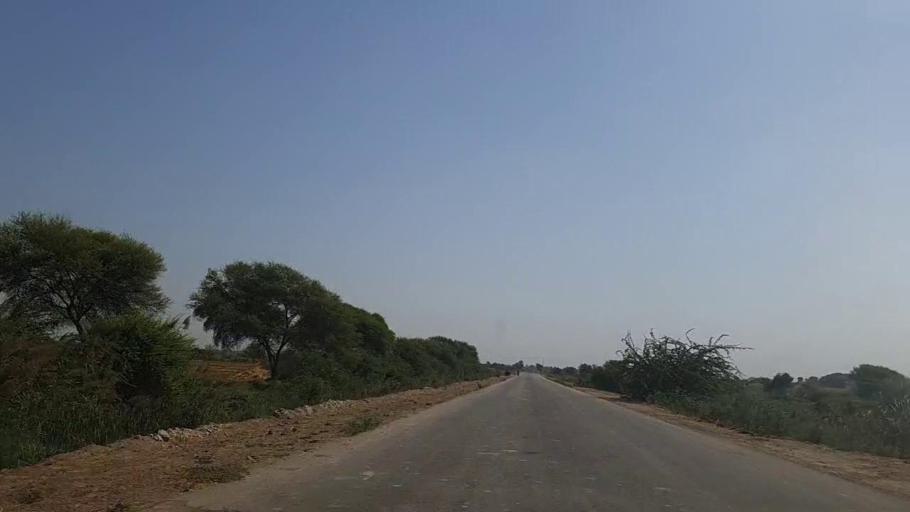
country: PK
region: Sindh
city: Daro Mehar
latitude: 24.7723
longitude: 68.2082
